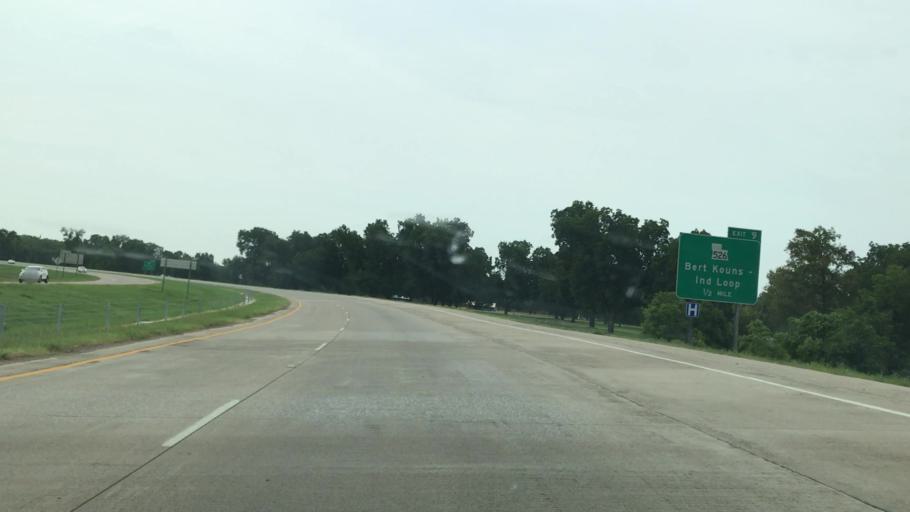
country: US
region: Louisiana
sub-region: Bossier Parish
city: Bossier City
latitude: 32.4051
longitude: -93.7145
